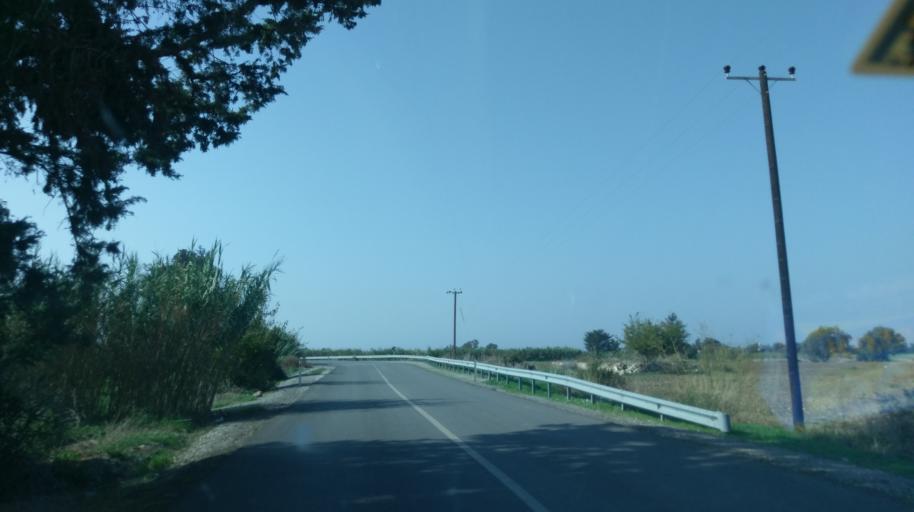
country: CY
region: Lefkosia
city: Morfou
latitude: 35.2104
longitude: 32.9680
